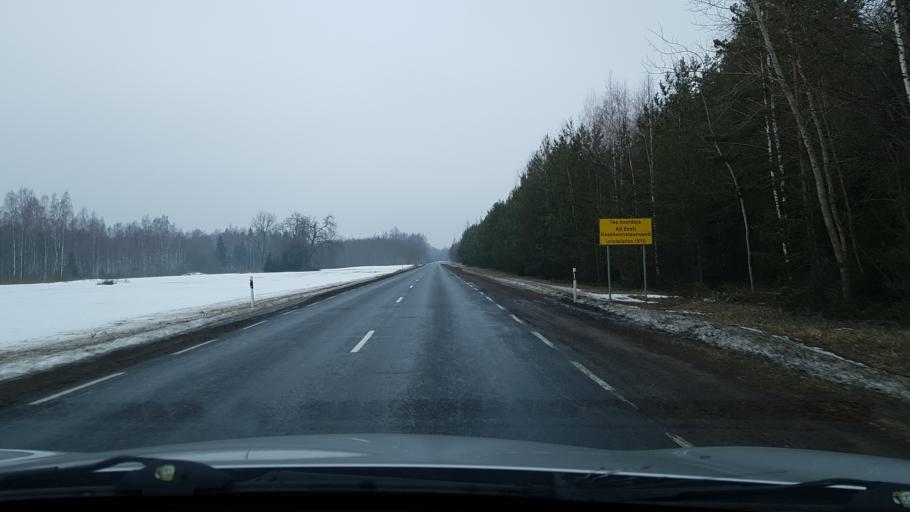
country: EE
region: Valgamaa
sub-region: Torva linn
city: Torva
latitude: 58.1127
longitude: 26.0012
